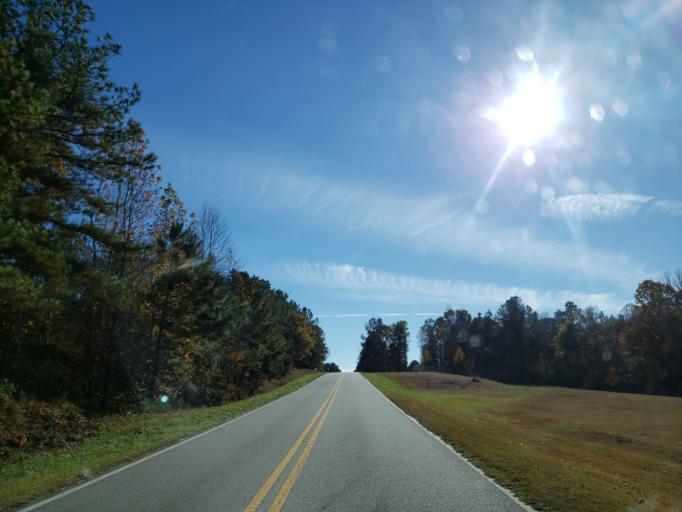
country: US
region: Alabama
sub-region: Cleburne County
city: Heflin
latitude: 33.5881
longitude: -85.6372
